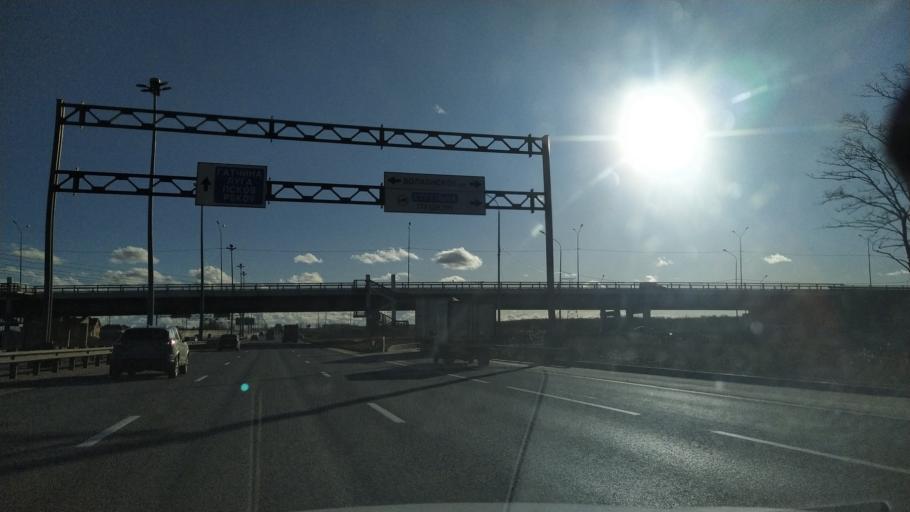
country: RU
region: St.-Petersburg
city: Aleksandrovskaya
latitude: 59.7455
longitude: 30.3106
